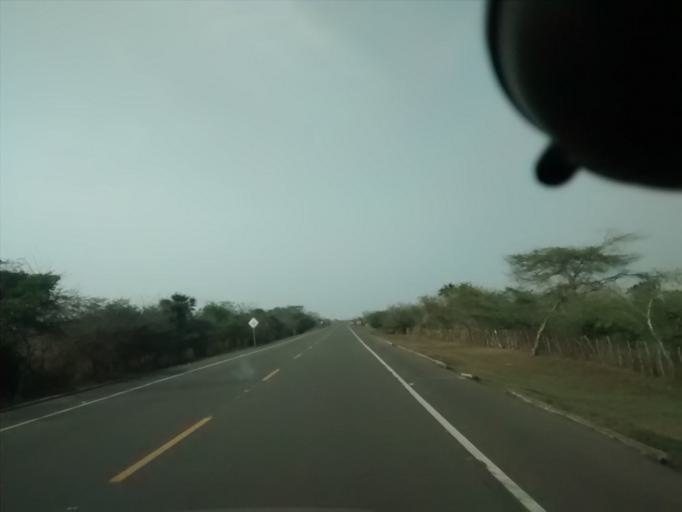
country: CO
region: Atlantico
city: Piojo
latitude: 10.7505
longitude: -75.2494
